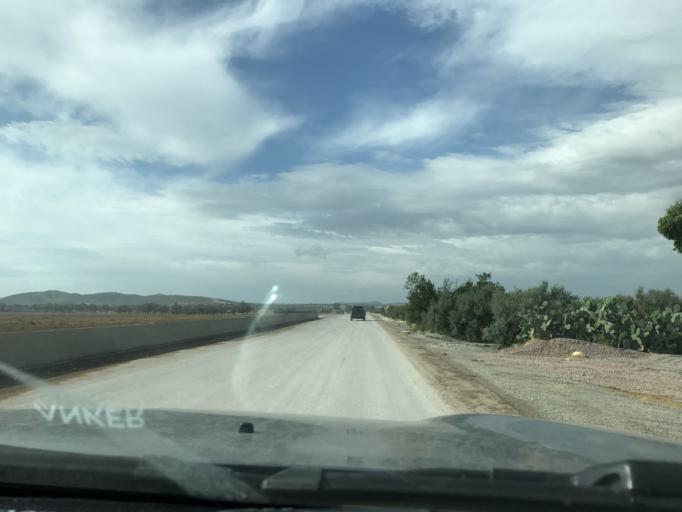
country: TN
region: Zaghwan
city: El Fahs
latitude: 36.3203
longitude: 9.8290
